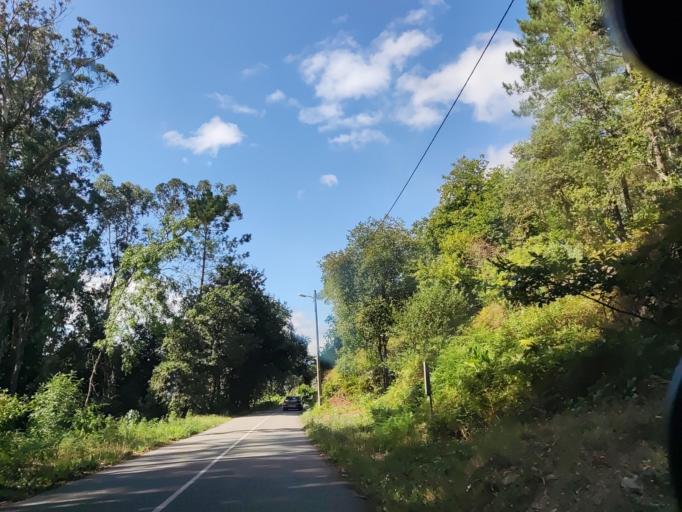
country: ES
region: Galicia
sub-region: Provincia da Coruna
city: Boiro
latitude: 42.6232
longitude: -8.8729
